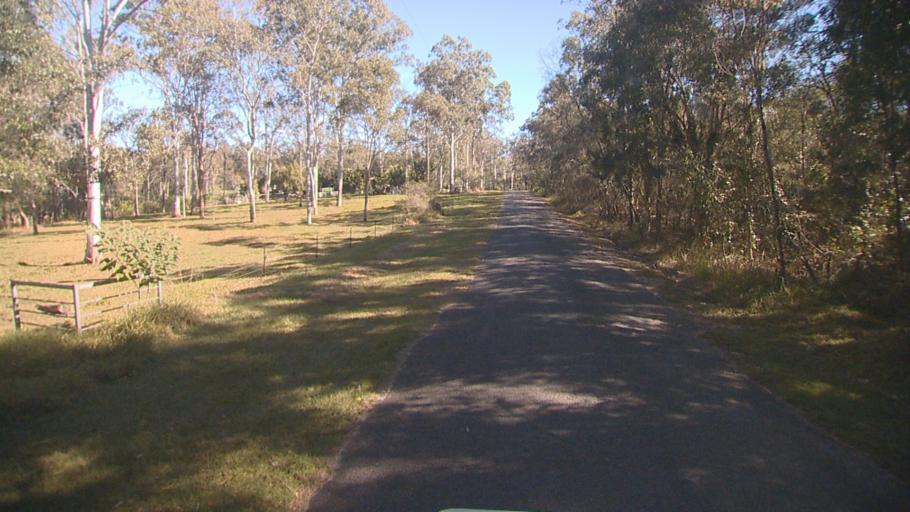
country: AU
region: Queensland
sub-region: Ipswich
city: Springfield Lakes
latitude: -27.7147
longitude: 152.9397
